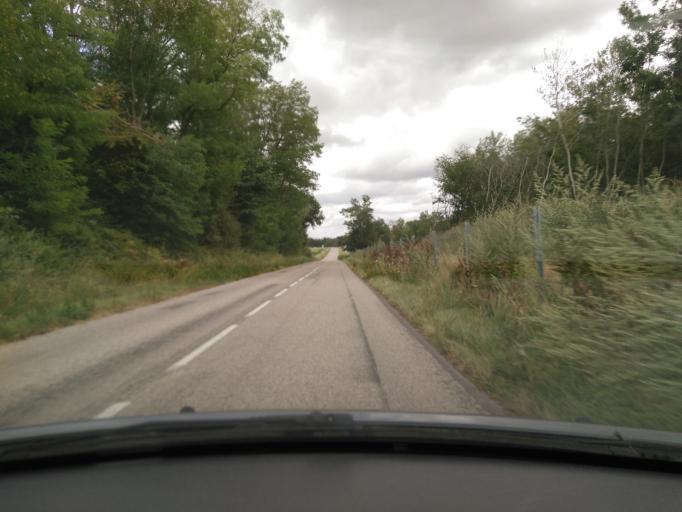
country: FR
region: Rhone-Alpes
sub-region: Departement de l'Isere
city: Beaurepaire
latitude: 45.4023
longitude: 5.0880
